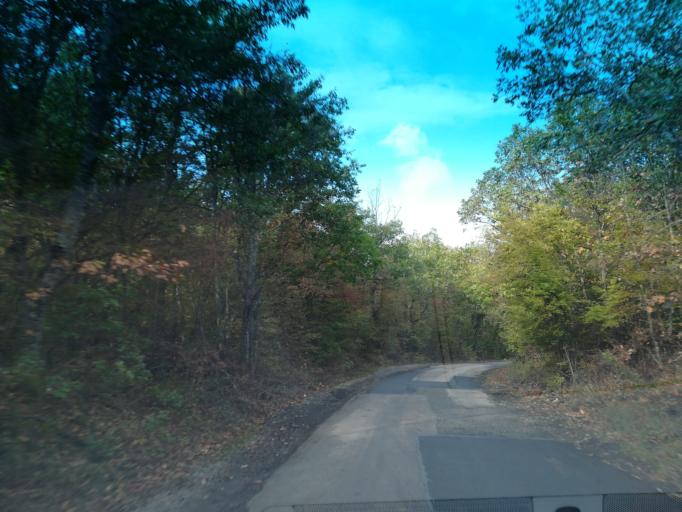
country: BG
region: Stara Zagora
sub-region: Obshtina Nikolaevo
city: Elkhovo
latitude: 42.3220
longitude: 25.4005
